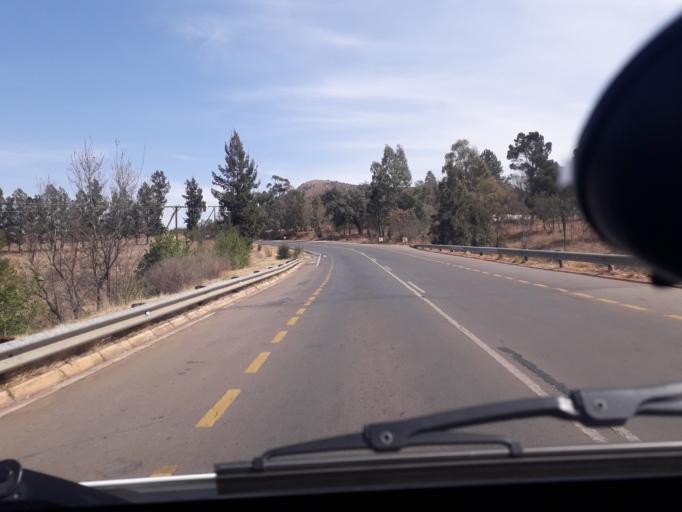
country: ZA
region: Gauteng
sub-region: West Rand District Municipality
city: Muldersdriseloop
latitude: -25.9892
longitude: 27.8426
